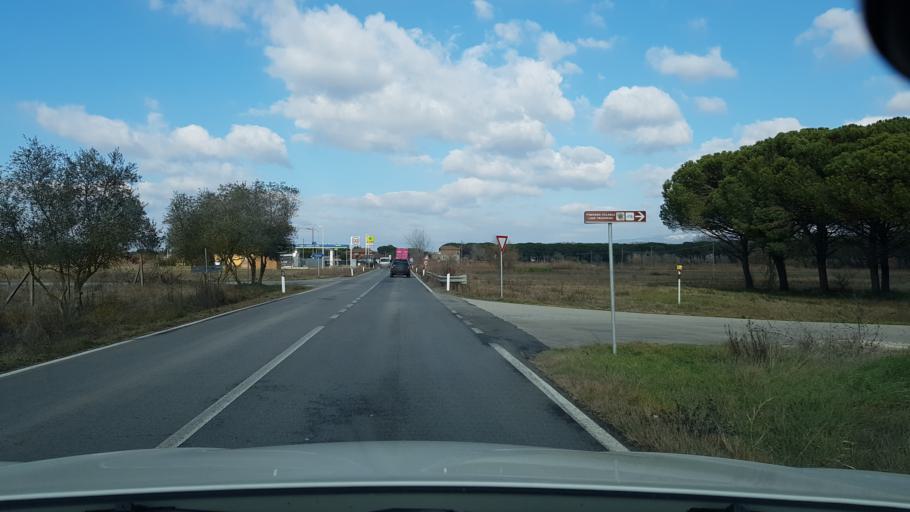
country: IT
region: Umbria
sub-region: Provincia di Perugia
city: Castiglione del Lago
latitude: 43.1480
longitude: 12.0230
